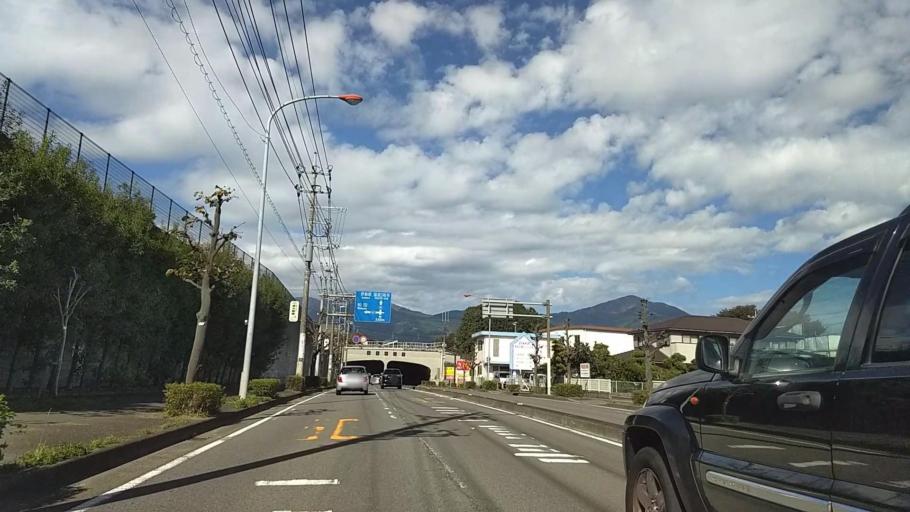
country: JP
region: Kanagawa
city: Hadano
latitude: 35.3585
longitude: 139.2347
